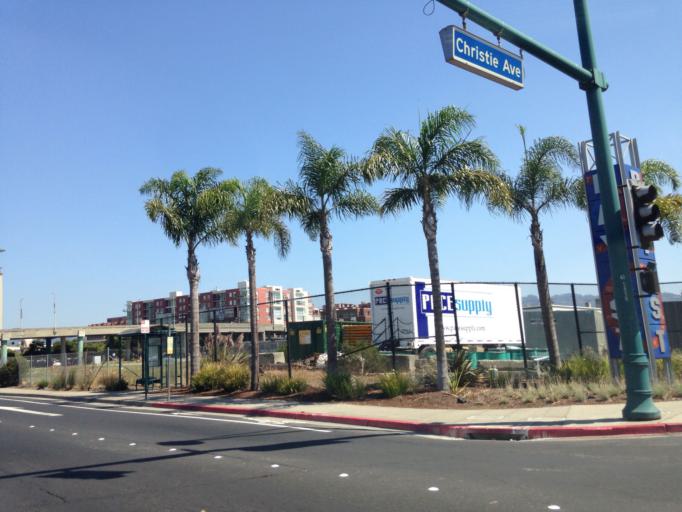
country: US
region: California
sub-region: Alameda County
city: Emeryville
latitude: 37.8371
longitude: -122.2931
